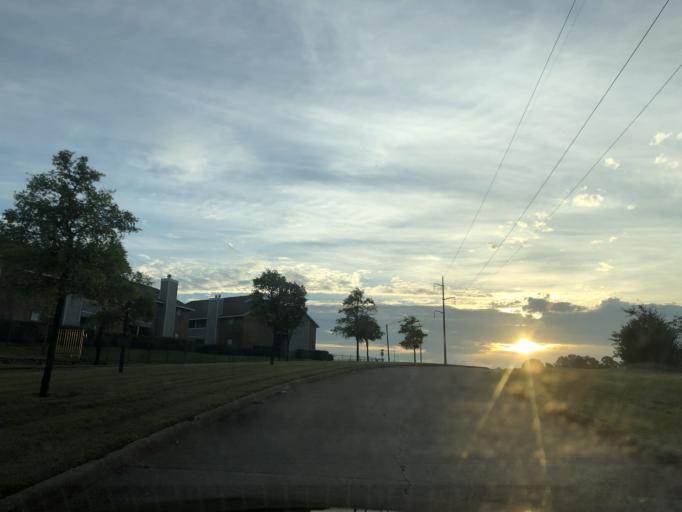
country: US
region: Texas
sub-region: Dallas County
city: Garland
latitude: 32.8407
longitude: -96.6212
